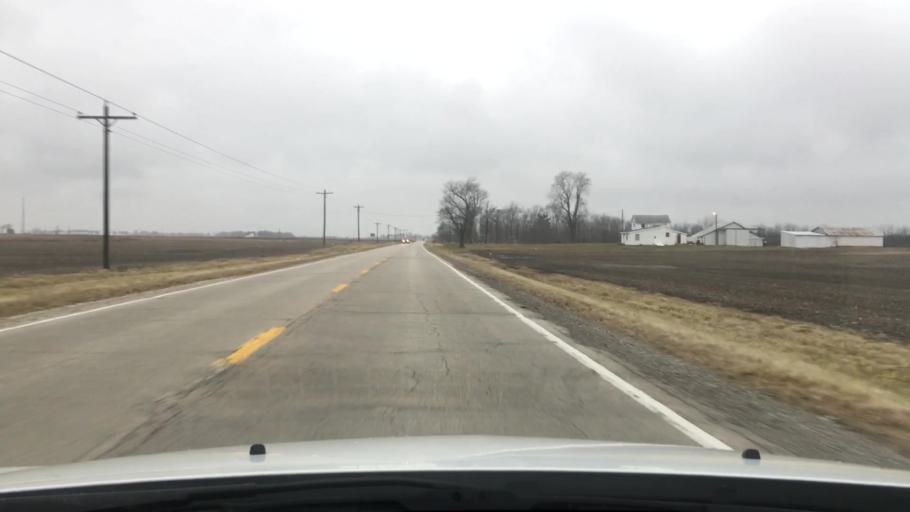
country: US
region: Illinois
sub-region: Iroquois County
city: Watseka
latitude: 40.8903
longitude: -87.7169
